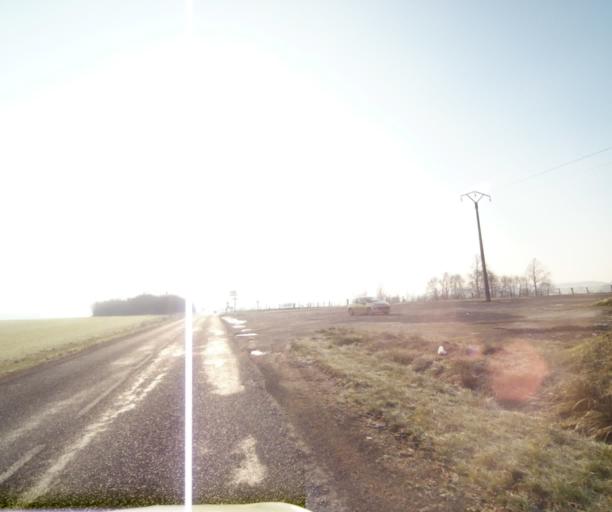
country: FR
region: Champagne-Ardenne
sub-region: Departement de la Haute-Marne
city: Montier-en-Der
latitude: 48.4962
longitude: 4.7536
